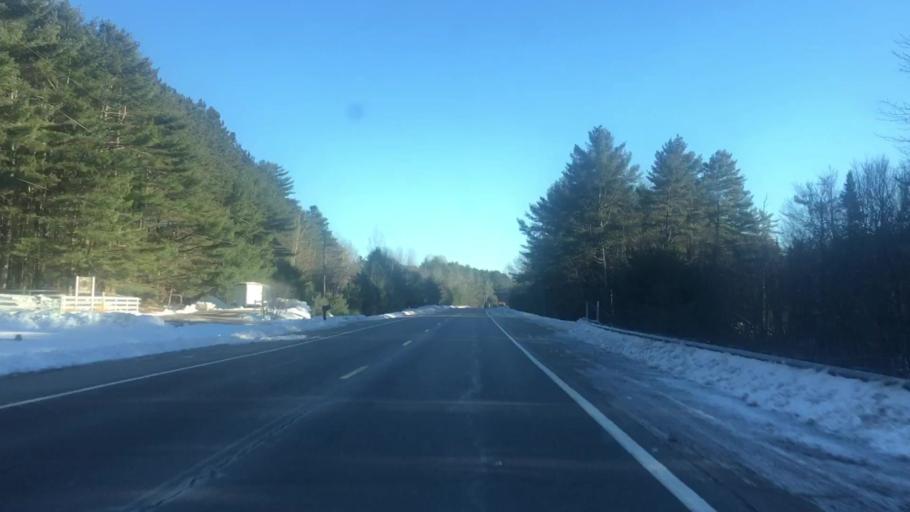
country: US
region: Maine
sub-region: Somerset County
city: Norridgewock
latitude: 44.6881
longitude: -69.7360
